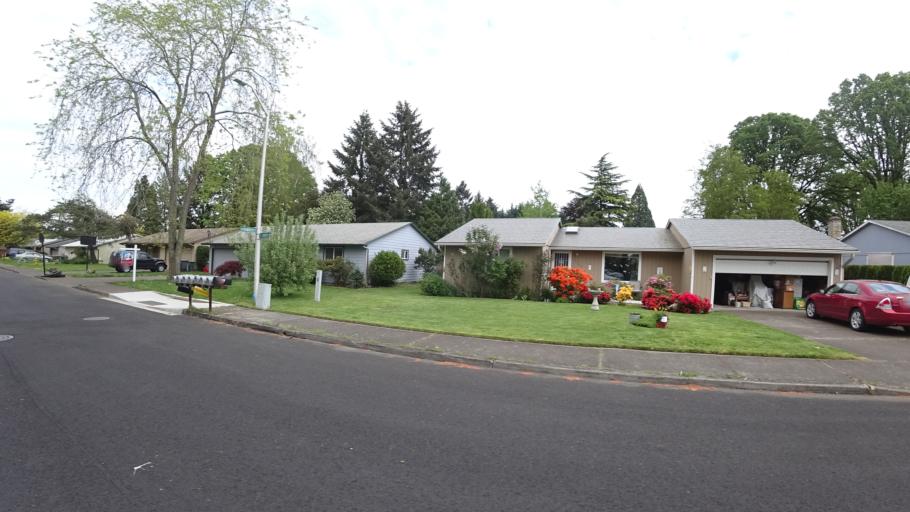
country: US
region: Oregon
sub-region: Washington County
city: Hillsboro
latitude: 45.4925
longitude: -122.9632
